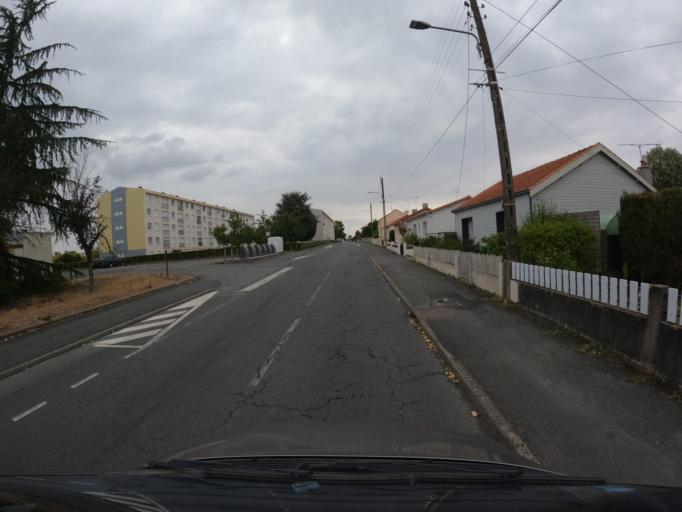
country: FR
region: Pays de la Loire
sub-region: Departement de la Vendee
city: Montaigu
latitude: 46.9801
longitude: -1.3072
